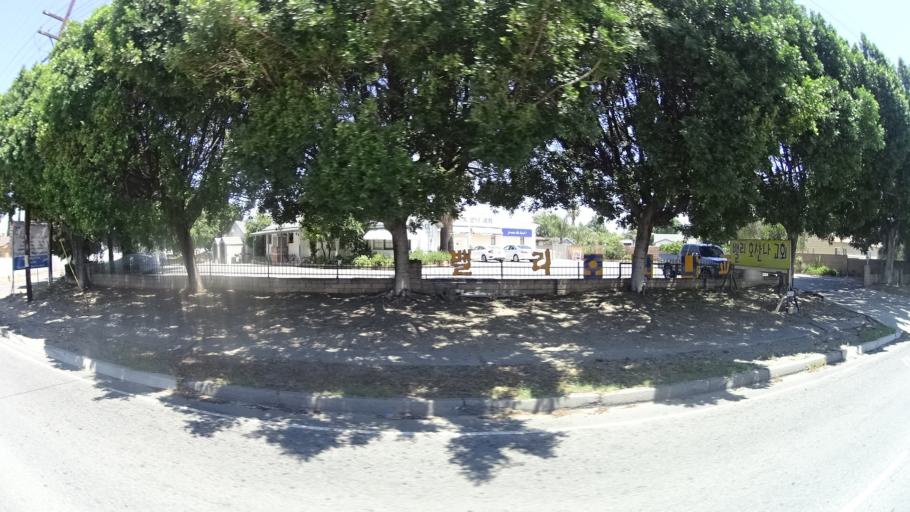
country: US
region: California
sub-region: Los Angeles County
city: San Fernando
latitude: 34.2354
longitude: -118.4438
